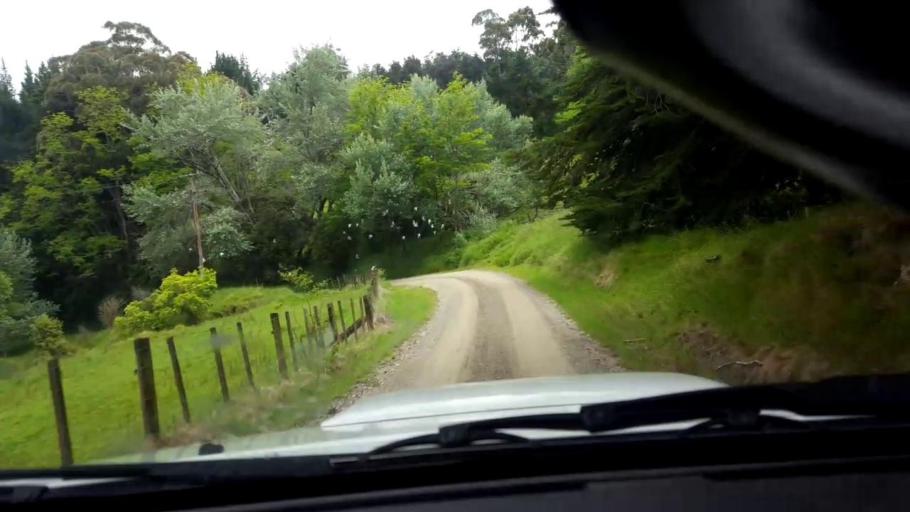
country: NZ
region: Gisborne
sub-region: Gisborne District
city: Gisborne
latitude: -38.3841
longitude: 177.6294
